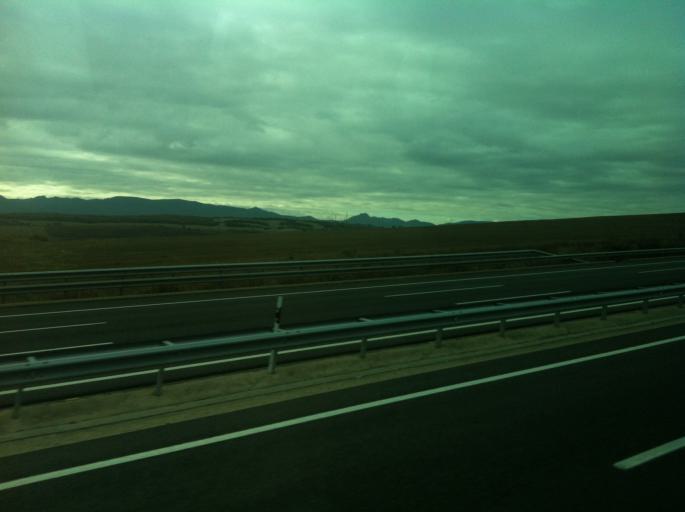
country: ES
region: Basque Country
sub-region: Provincia de Alava
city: Arminon
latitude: 42.7077
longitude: -2.8877
